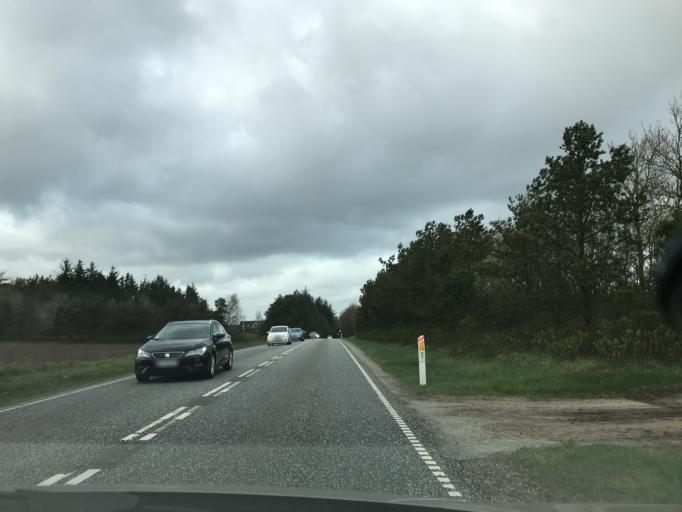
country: DK
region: Central Jutland
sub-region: Skive Kommune
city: Skive
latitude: 56.5107
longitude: 8.9534
